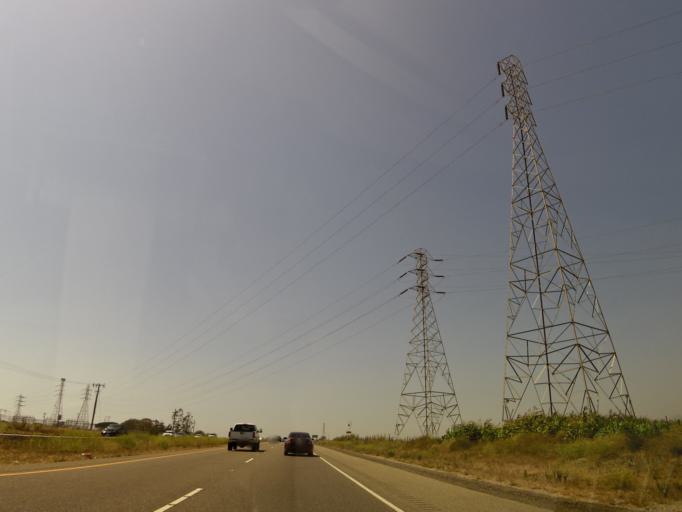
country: US
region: California
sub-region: San Luis Obispo County
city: Nipomo
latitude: 35.0074
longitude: -120.4460
